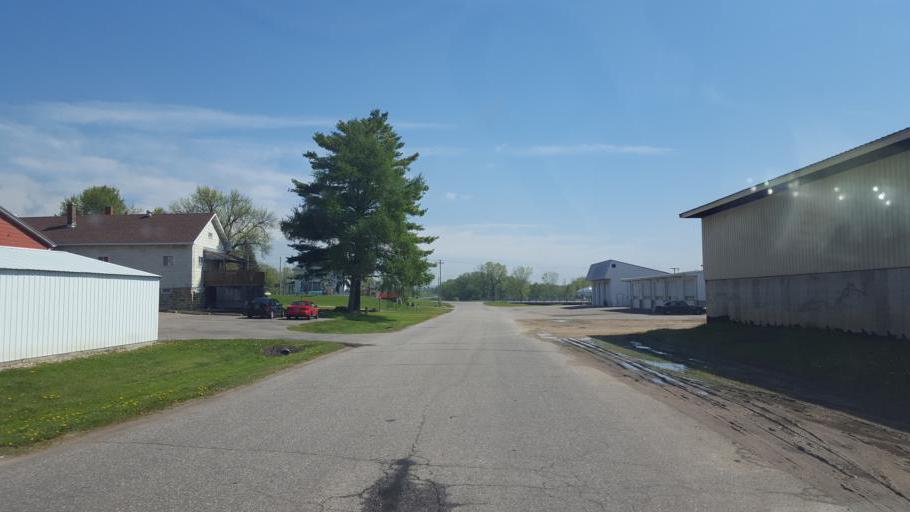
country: US
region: Wisconsin
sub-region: Vernon County
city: Hillsboro
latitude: 43.6519
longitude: -90.3376
